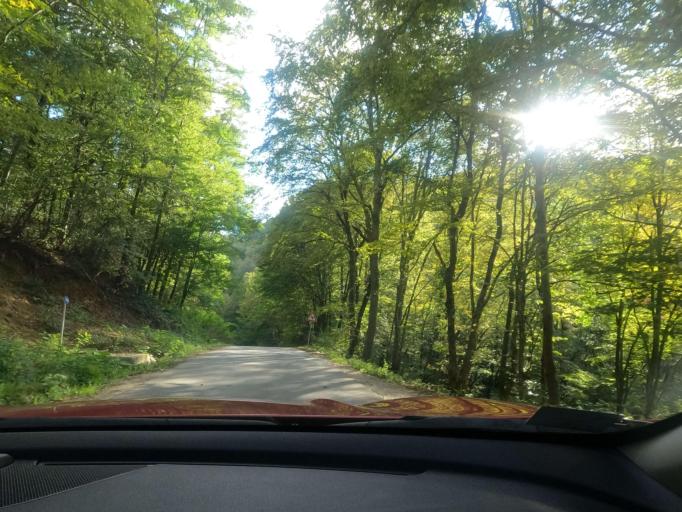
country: HR
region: Sisacko-Moslavacka
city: Petrinja
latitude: 45.4091
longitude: 16.2477
